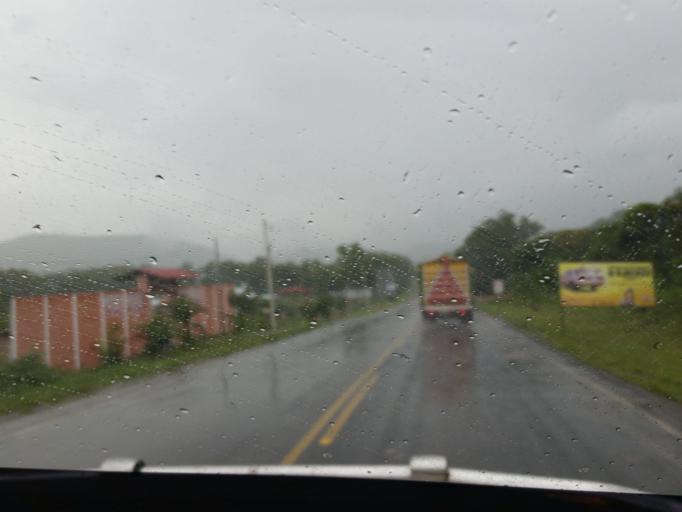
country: NI
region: Matagalpa
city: Matagalpa
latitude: 12.9188
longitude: -85.9724
